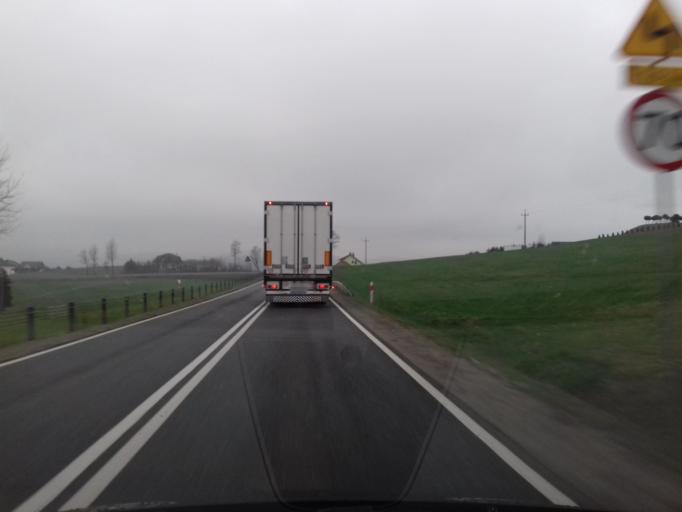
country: PL
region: Lesser Poland Voivodeship
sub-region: Powiat limanowski
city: Lukowica
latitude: 49.6525
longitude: 20.5538
